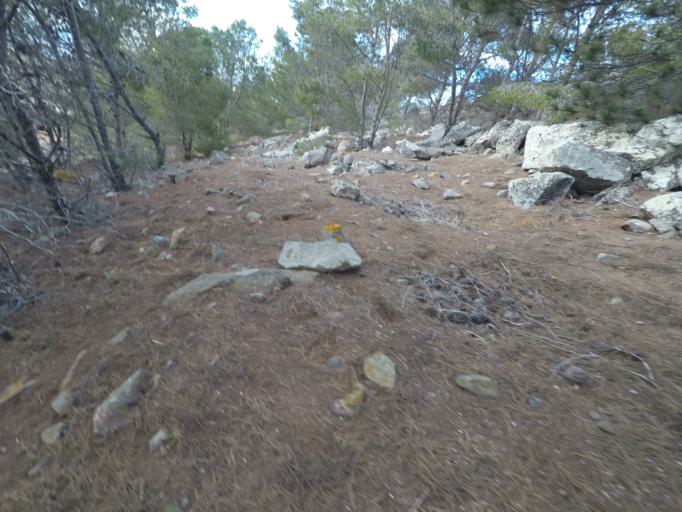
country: PT
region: Madeira
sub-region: Porto Santo
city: Vila de Porto Santo
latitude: 33.0444
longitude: -16.3710
